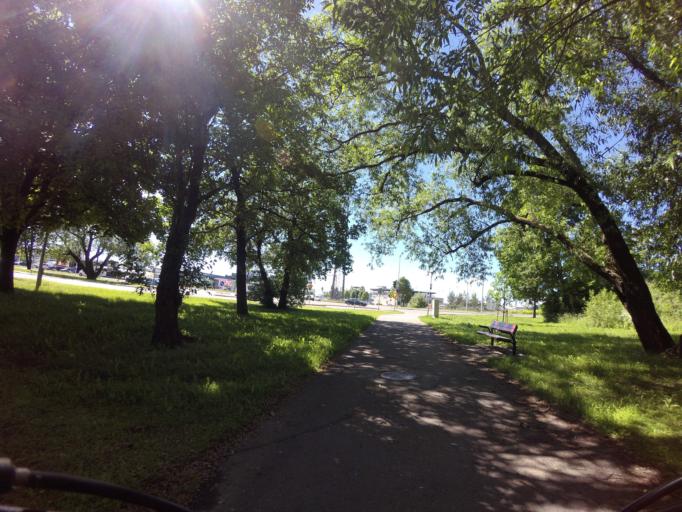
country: FI
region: Varsinais-Suomi
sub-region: Turku
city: Turku
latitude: 60.4448
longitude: 22.2255
